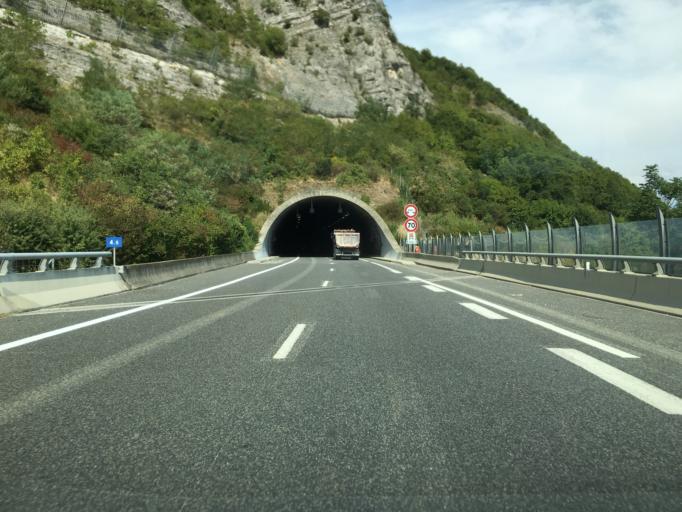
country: FR
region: Rhone-Alpes
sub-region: Departement de l'Isere
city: Allieres-et-Risset
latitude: 45.0803
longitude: 5.6794
